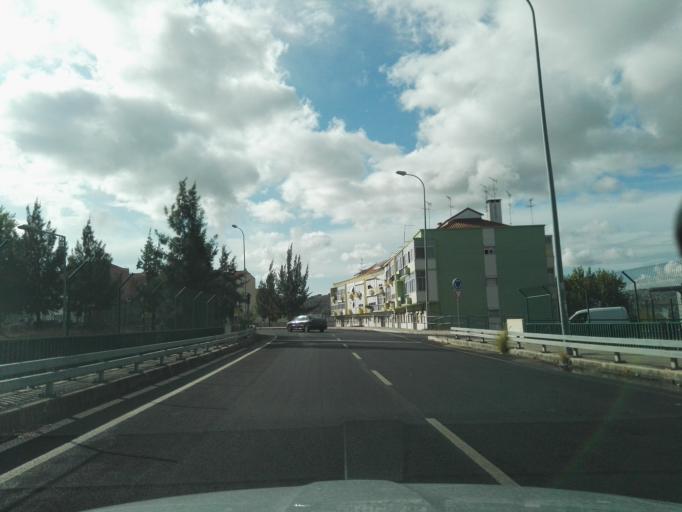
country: PT
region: Lisbon
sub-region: Odivelas
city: Pontinha
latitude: 38.7574
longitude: -9.2050
